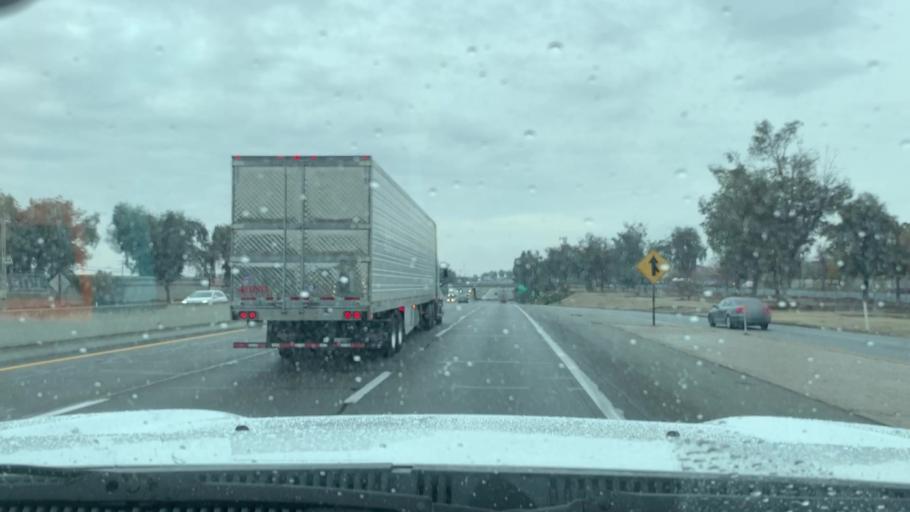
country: US
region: California
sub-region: Kern County
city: Delano
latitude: 35.7731
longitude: -119.2516
